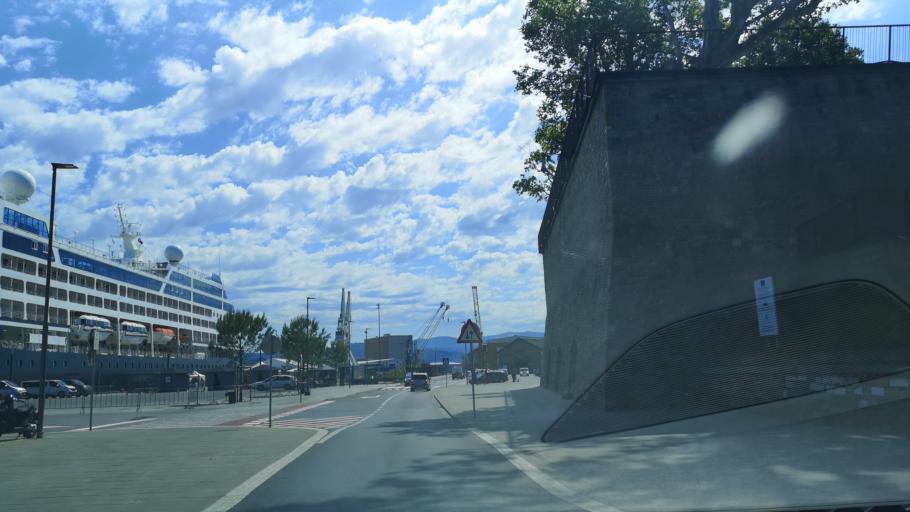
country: SI
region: Koper-Capodistria
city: Koper
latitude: 45.5499
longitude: 13.7289
